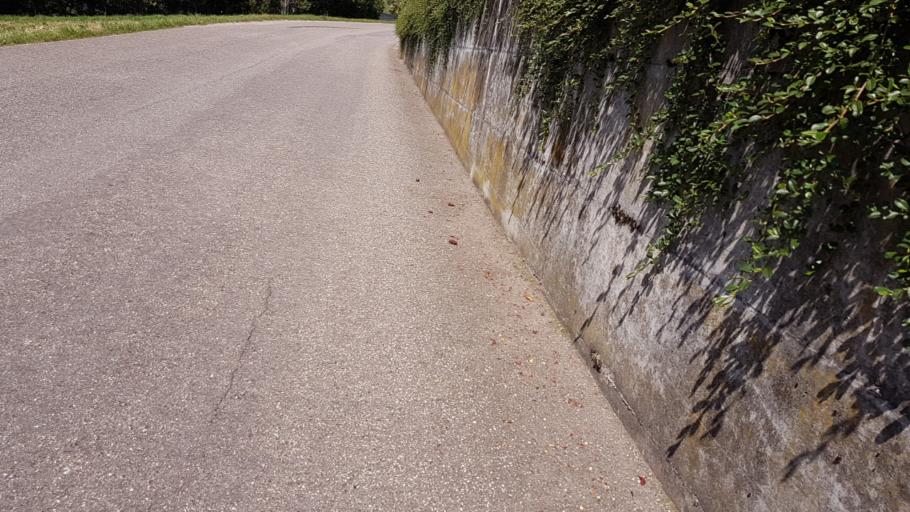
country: CH
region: Lucerne
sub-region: Entlebuch District
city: Oberdiessbach
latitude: 46.8461
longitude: 7.6222
